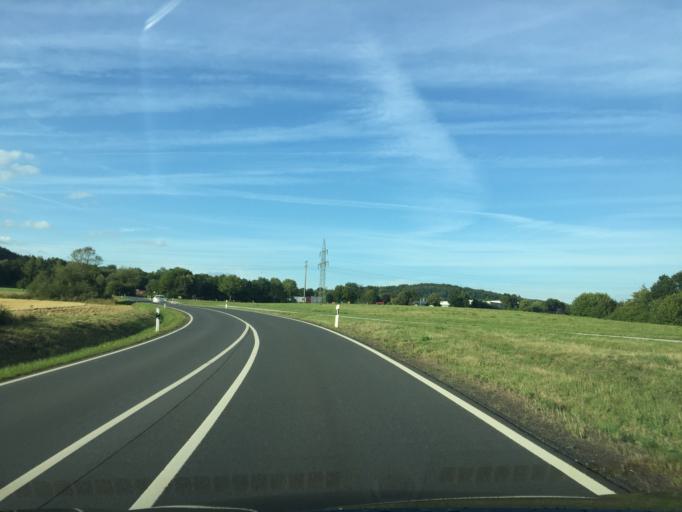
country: DE
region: Rheinland-Pfalz
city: Heiligenroth
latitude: 50.4567
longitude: 7.8702
